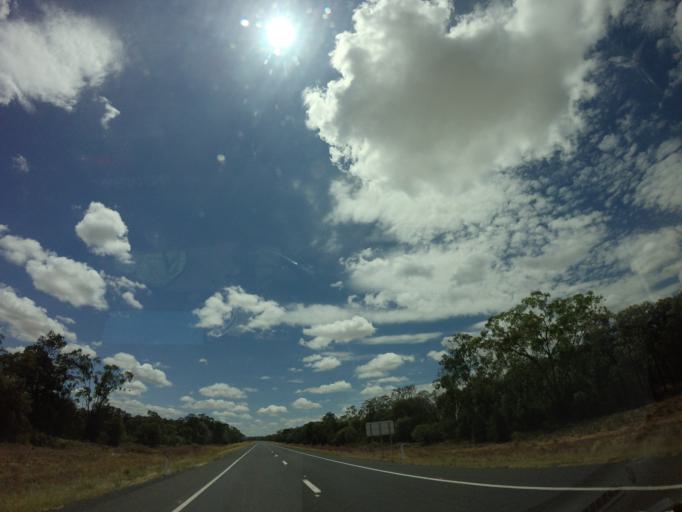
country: AU
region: New South Wales
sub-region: Moree Plains
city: Boggabilla
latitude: -28.8635
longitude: 150.2034
